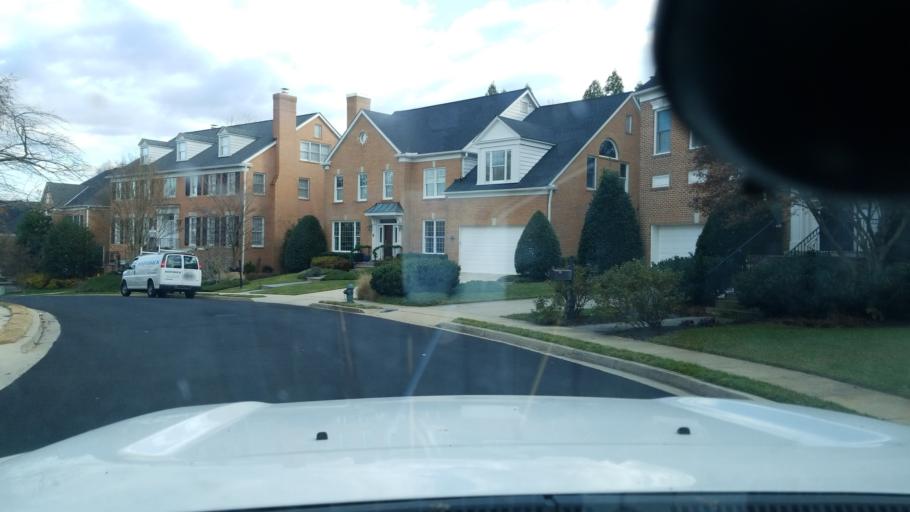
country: US
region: Maryland
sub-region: Montgomery County
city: Brookmont
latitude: 38.9438
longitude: -77.1001
